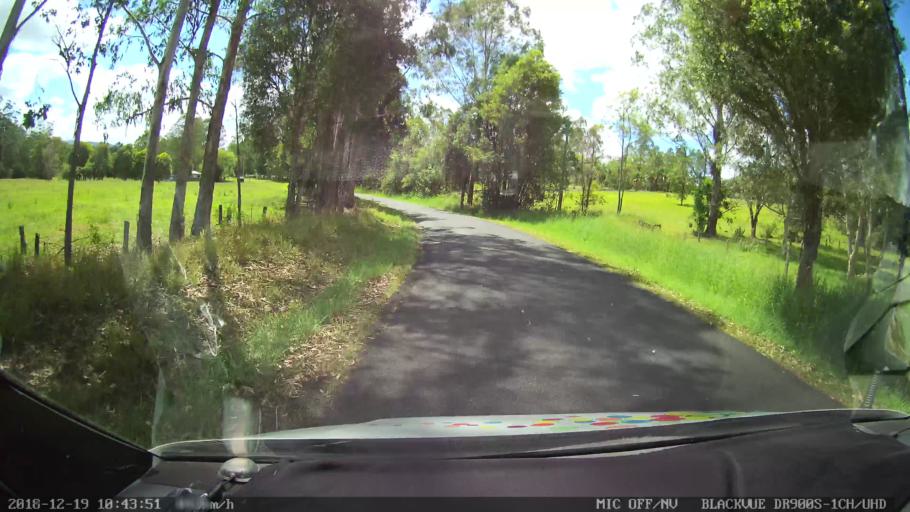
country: AU
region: New South Wales
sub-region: Lismore Municipality
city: Nimbin
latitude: -28.5960
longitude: 153.1759
